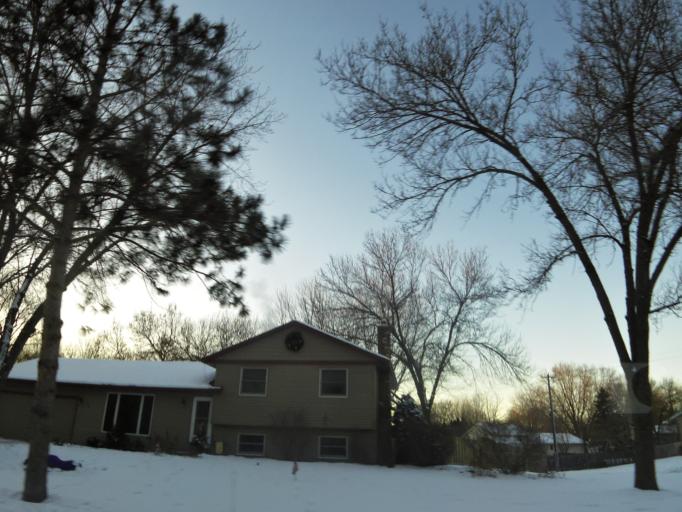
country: US
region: Minnesota
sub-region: Washington County
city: Stillwater
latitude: 45.0538
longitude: -92.8414
